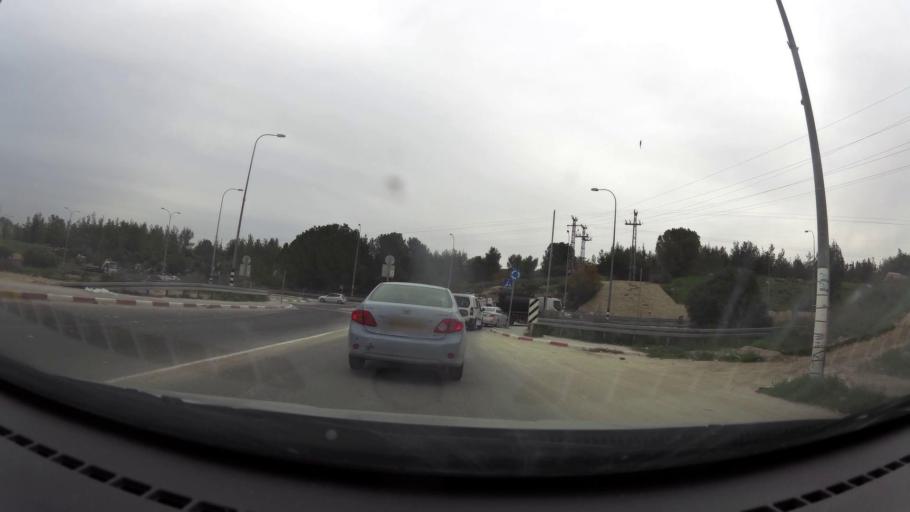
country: IL
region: Jerusalem
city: Bet Shemesh
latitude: 31.7034
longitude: 35.0085
